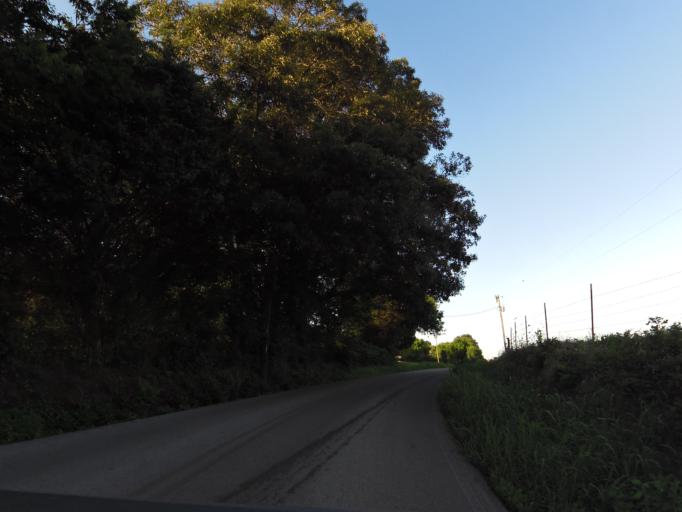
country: US
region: Tennessee
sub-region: Loudon County
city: Greenback
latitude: 35.7174
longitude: -84.2120
